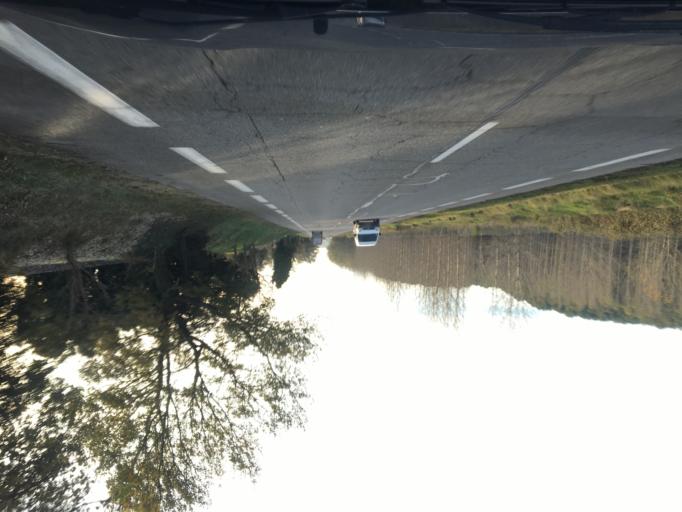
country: FR
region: Provence-Alpes-Cote d'Azur
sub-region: Departement du Vaucluse
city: Lauris
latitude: 43.7499
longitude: 5.2754
